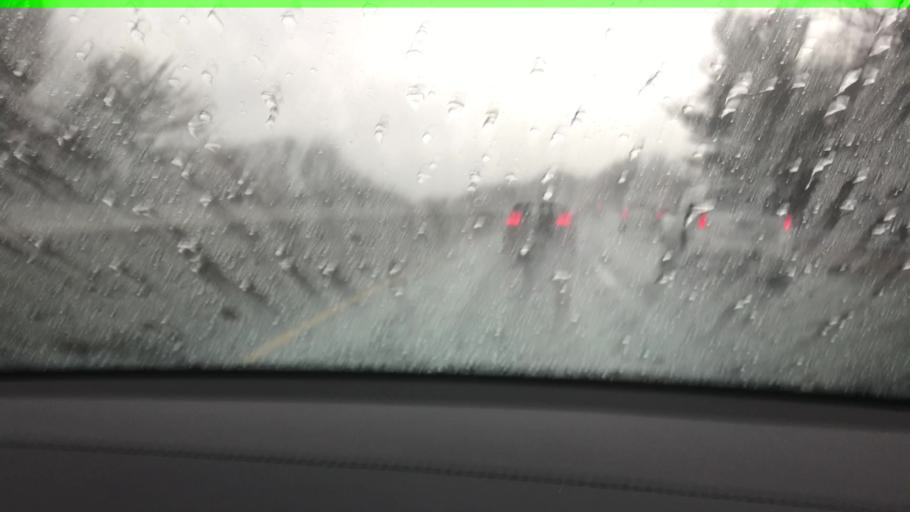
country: US
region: Connecticut
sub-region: New Haven County
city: Hamden
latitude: 41.3672
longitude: -72.9174
